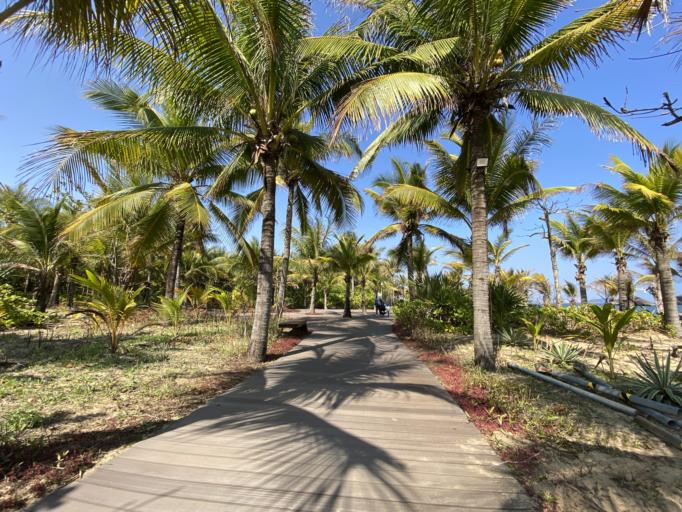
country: CN
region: Hainan
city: Haitangwan
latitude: 18.3484
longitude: 109.7400
